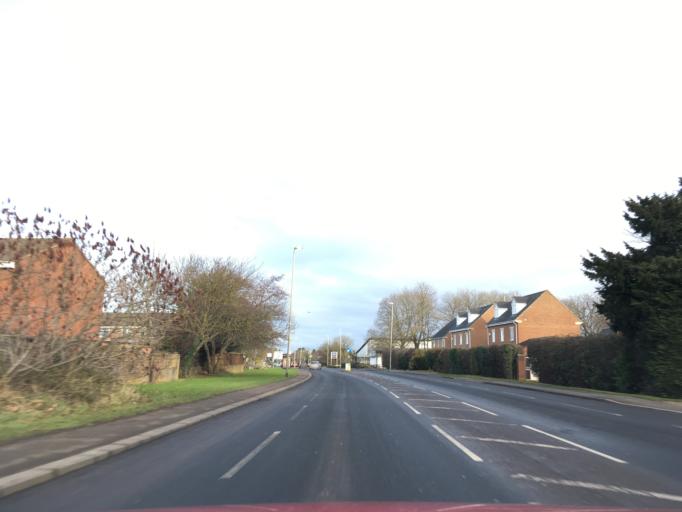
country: GB
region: England
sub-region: Gloucestershire
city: Gloucester
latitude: 51.8246
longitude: -2.2773
